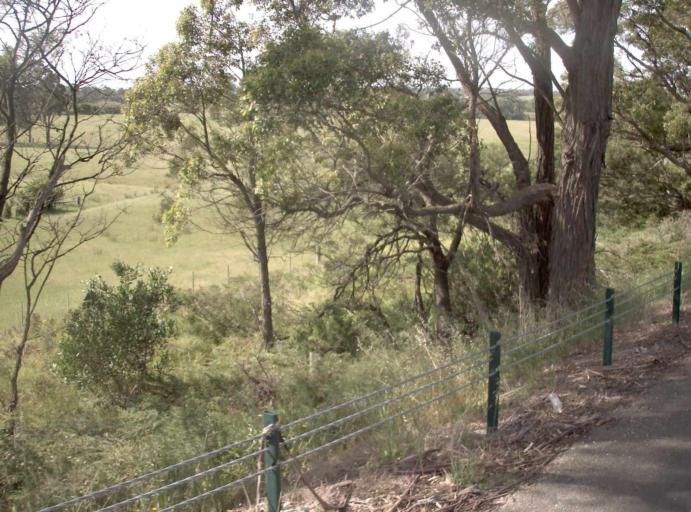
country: AU
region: Victoria
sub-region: East Gippsland
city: Lakes Entrance
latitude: -37.8603
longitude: 148.0286
